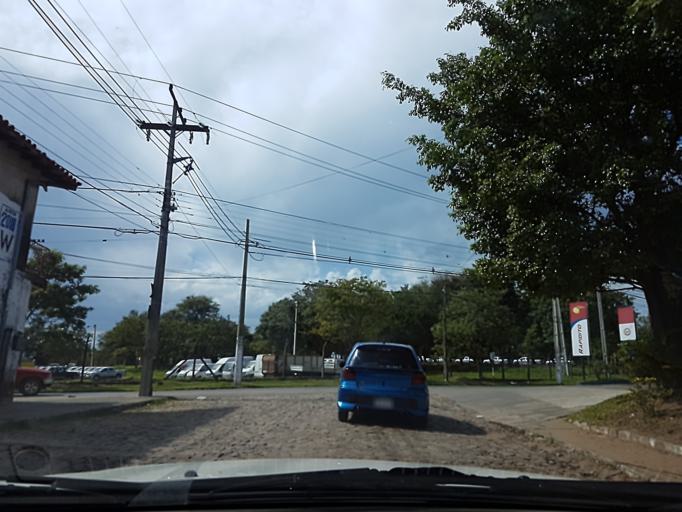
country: PY
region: Central
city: Colonia Mariano Roque Alonso
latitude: -25.2328
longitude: -57.5706
